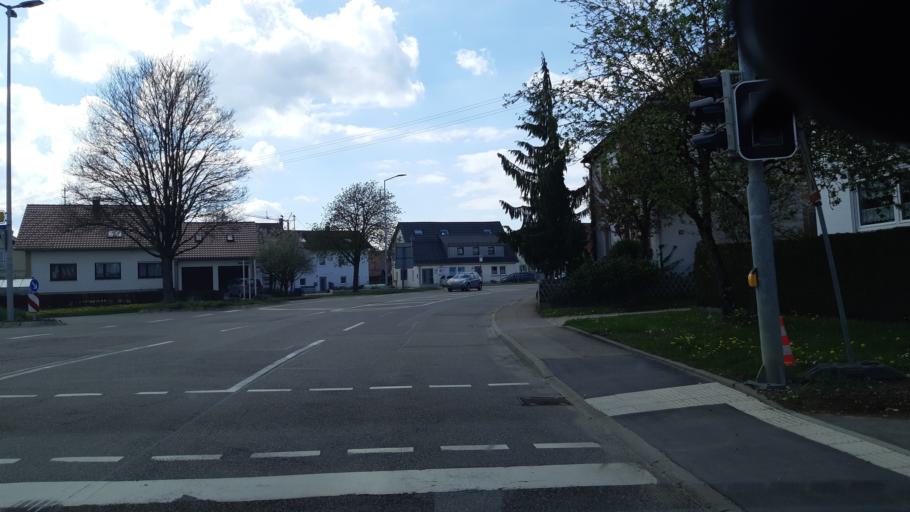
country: DE
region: Baden-Wuerttemberg
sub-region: Regierungsbezirk Stuttgart
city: Westhausen
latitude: 48.8038
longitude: 10.1846
